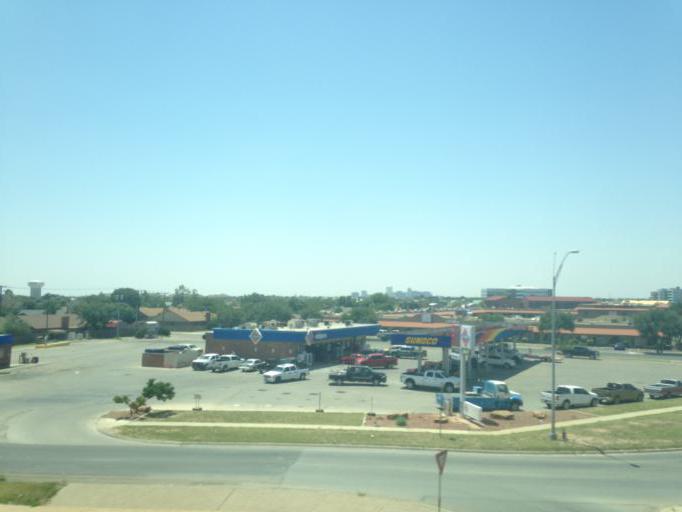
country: US
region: Texas
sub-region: Midland County
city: Midland
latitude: 32.0435
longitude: -102.0856
